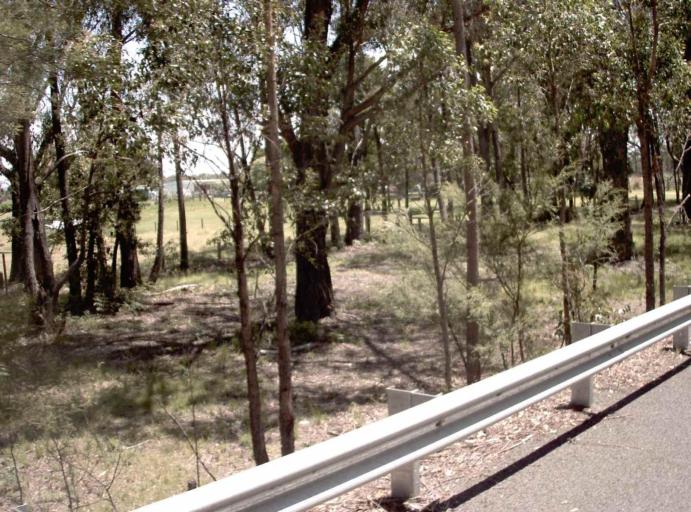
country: AU
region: Victoria
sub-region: East Gippsland
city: Lakes Entrance
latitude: -37.7797
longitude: 148.0509
